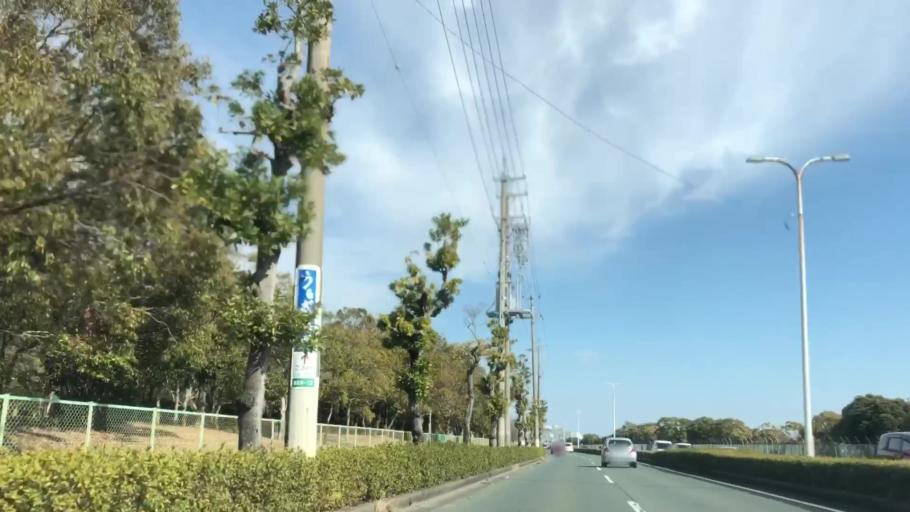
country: JP
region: Shizuoka
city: Hamamatsu
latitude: 34.7534
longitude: 137.7067
